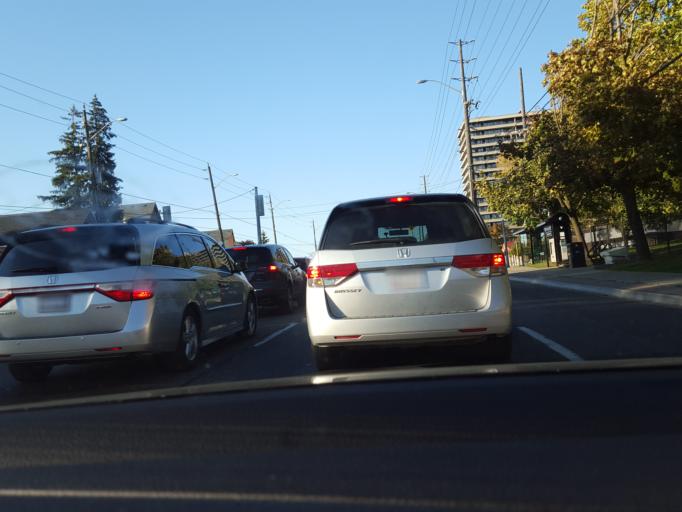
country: CA
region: Ontario
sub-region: York
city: Richmond Hill
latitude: 43.8223
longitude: -79.4257
